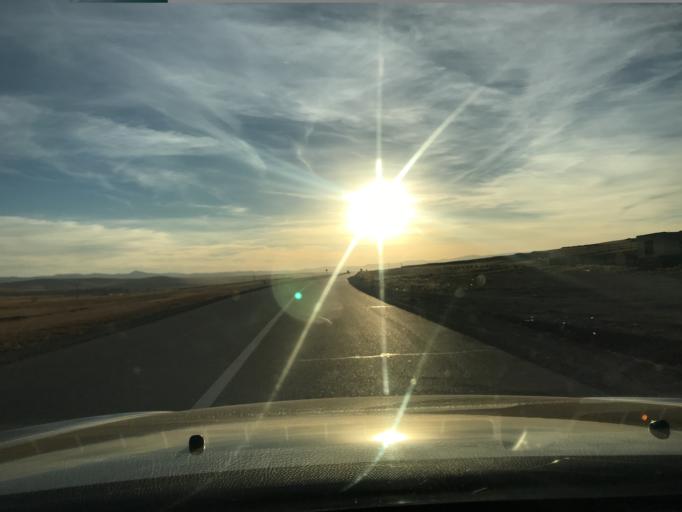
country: MN
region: Central Aimak
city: Arhust
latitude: 47.8034
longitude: 107.5263
